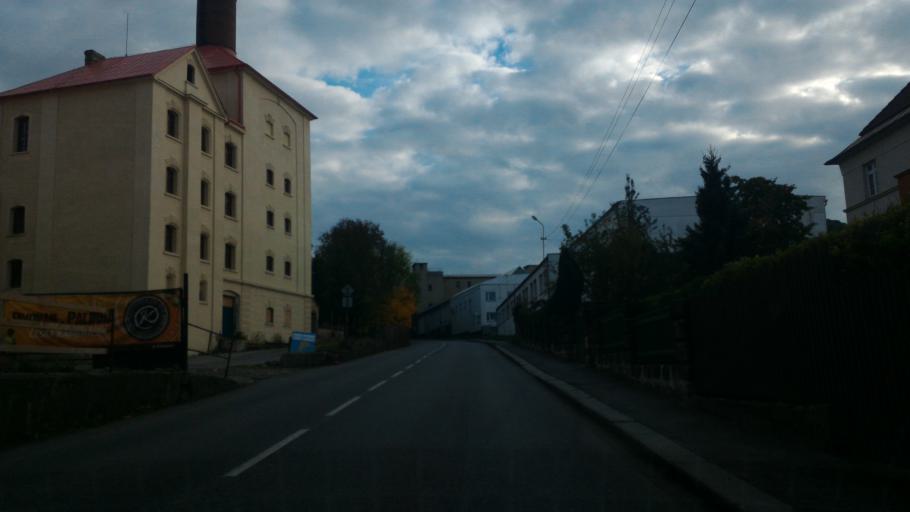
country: CZ
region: Ustecky
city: Ceska Kamenice
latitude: 50.7984
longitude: 14.4143
